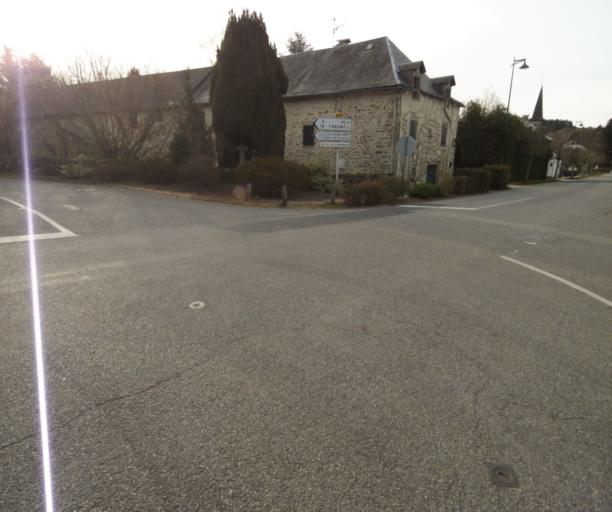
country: FR
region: Limousin
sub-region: Departement de la Correze
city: Treignac
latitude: 45.4741
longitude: 1.7913
